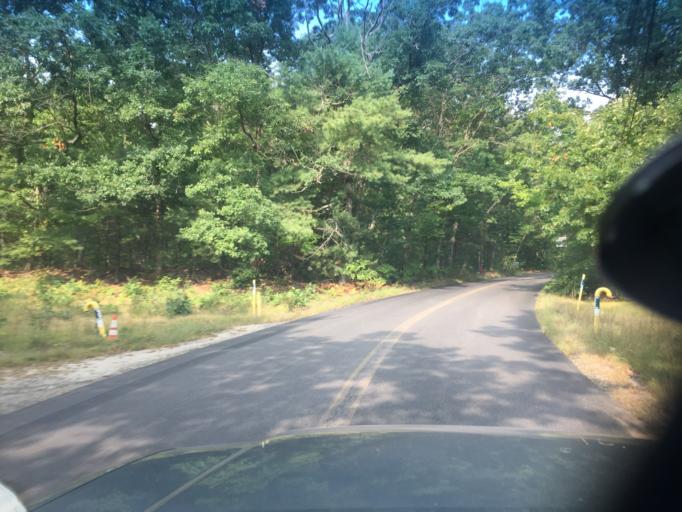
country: US
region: Massachusetts
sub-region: Norfolk County
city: Bellingham
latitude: 42.1305
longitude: -71.4598
